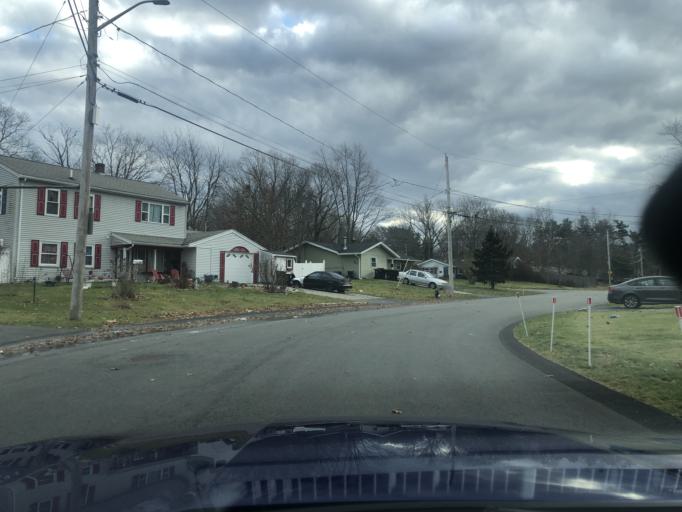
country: US
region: Massachusetts
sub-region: Plymouth County
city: Brockton
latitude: 42.1113
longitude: -71.0077
